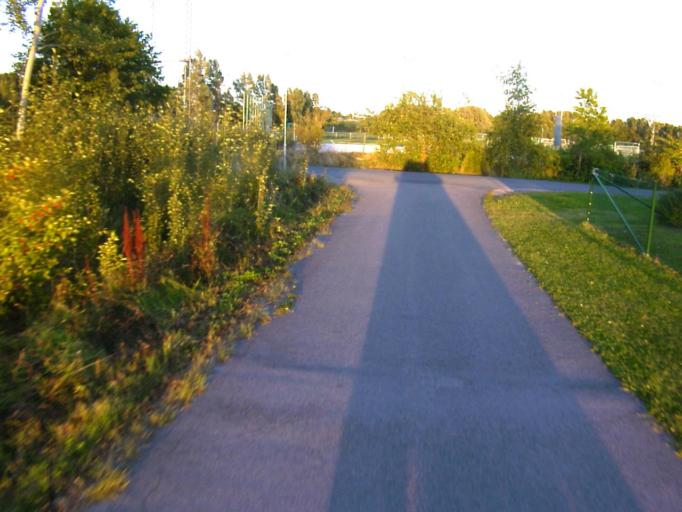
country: SE
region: Soedermanland
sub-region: Eskilstuna Kommun
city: Eskilstuna
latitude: 59.3866
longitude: 16.5176
